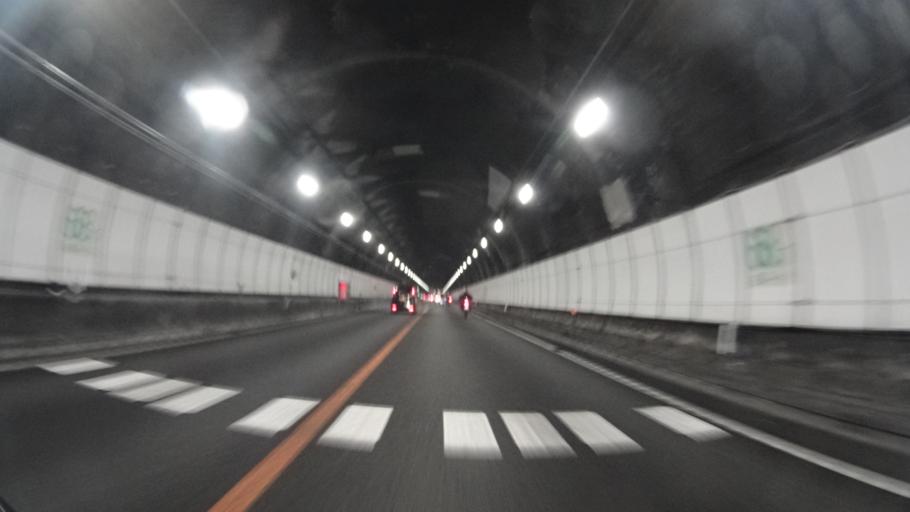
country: JP
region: Shizuoka
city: Gotemba
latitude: 35.3697
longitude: 139.0488
